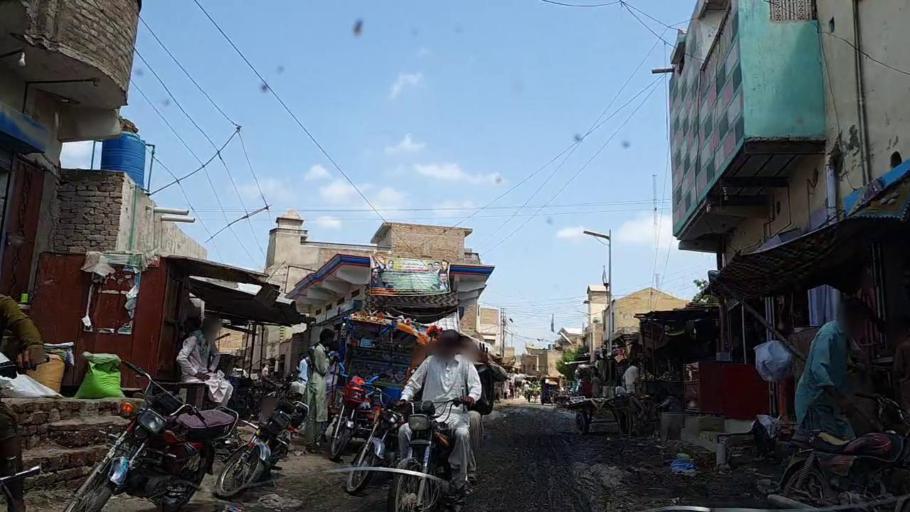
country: PK
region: Sindh
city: Tharu Shah
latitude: 26.9434
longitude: 68.1148
